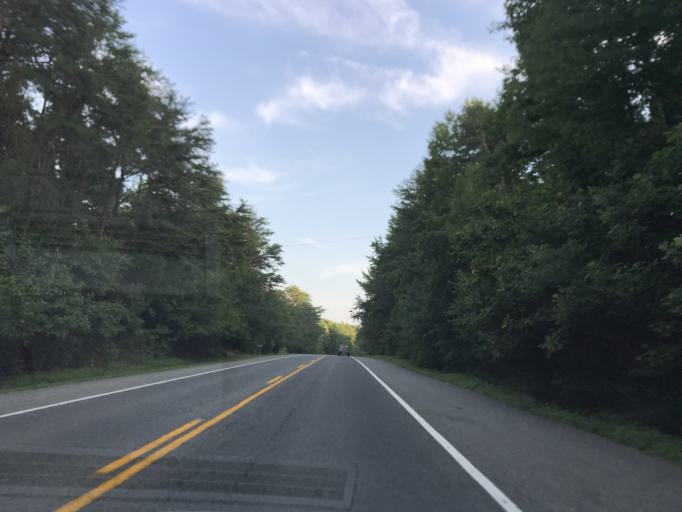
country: US
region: Maryland
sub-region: Cecil County
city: Charlestown
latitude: 39.5541
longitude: -75.9492
